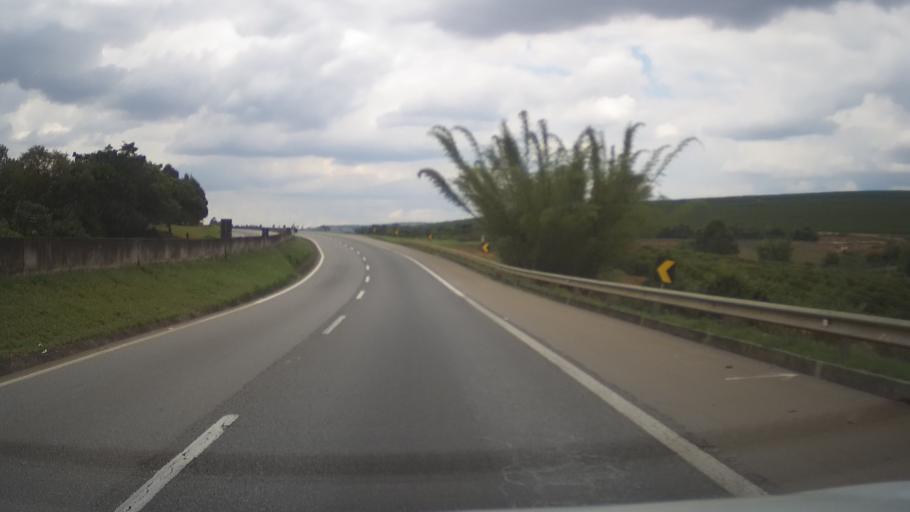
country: BR
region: Minas Gerais
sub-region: Tres Coracoes
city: Tres Coracoes
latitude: -21.5119
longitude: -45.2168
